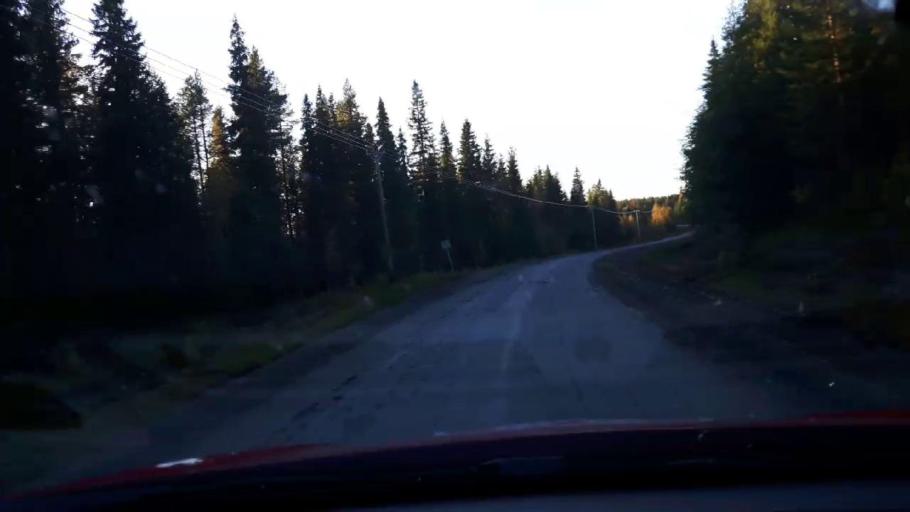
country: SE
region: Jaemtland
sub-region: Krokoms Kommun
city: Krokom
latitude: 63.4549
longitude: 14.5096
